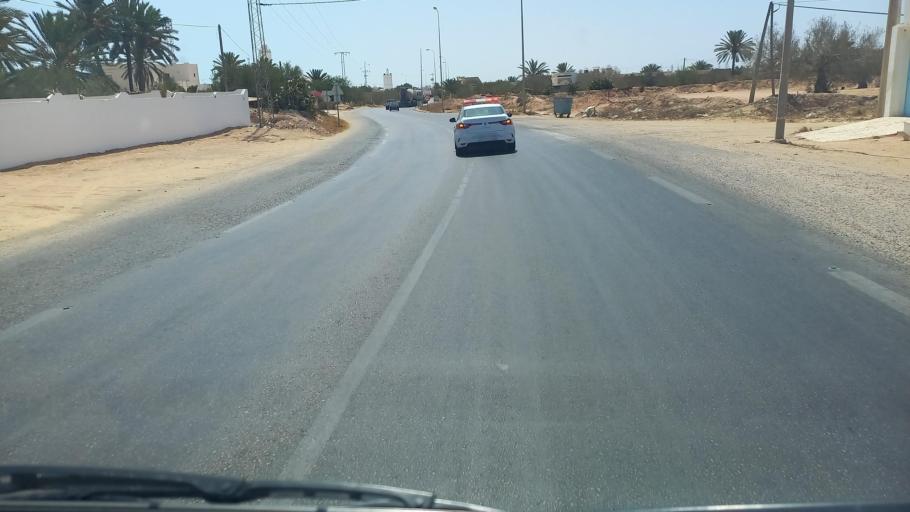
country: TN
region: Madanin
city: Houmt Souk
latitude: 33.7834
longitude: 10.8879
